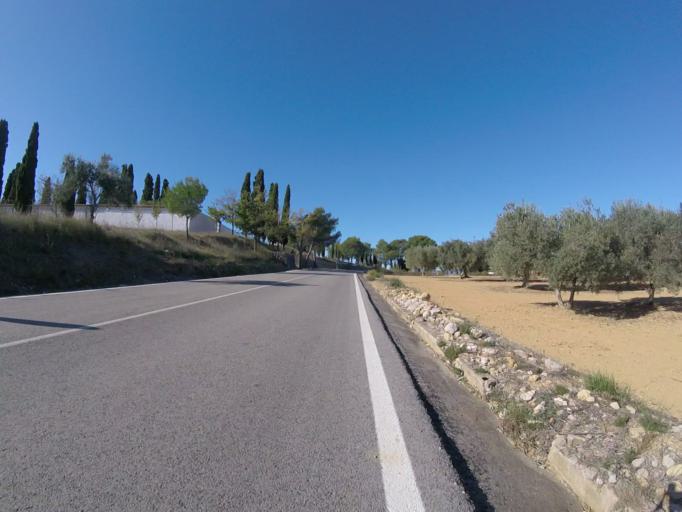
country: ES
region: Valencia
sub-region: Provincia de Castello
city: Chert/Xert
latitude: 40.4647
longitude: 0.1934
